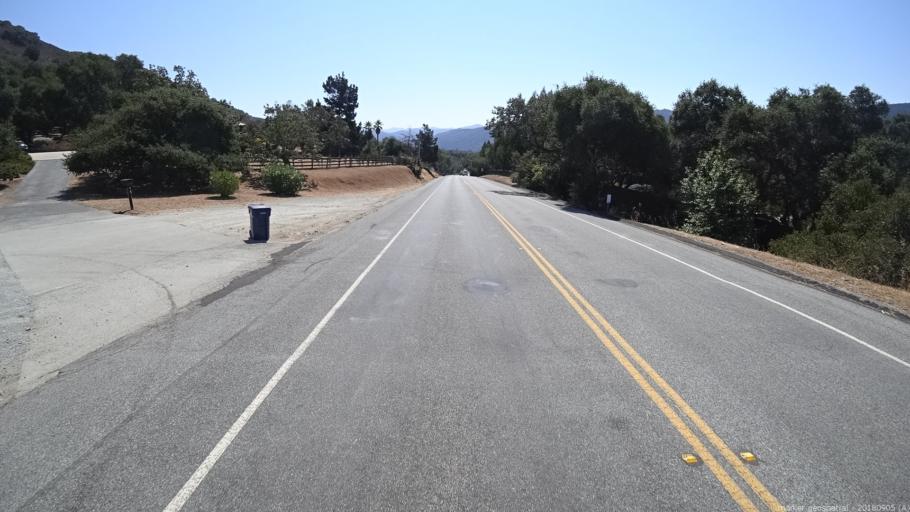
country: US
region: California
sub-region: Monterey County
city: Carmel Valley Village
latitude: 36.5103
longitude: -121.7543
